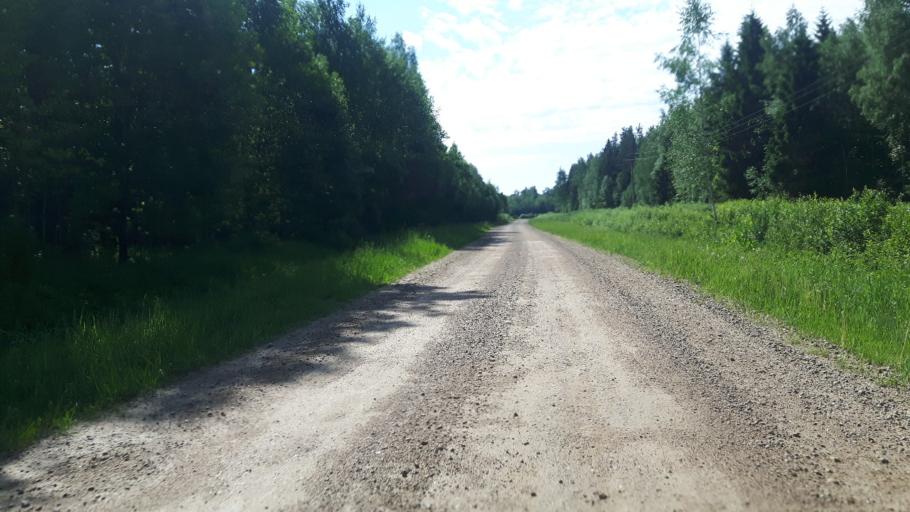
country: EE
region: Paernumaa
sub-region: Vaendra vald (alev)
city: Vandra
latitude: 58.6957
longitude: 25.0313
